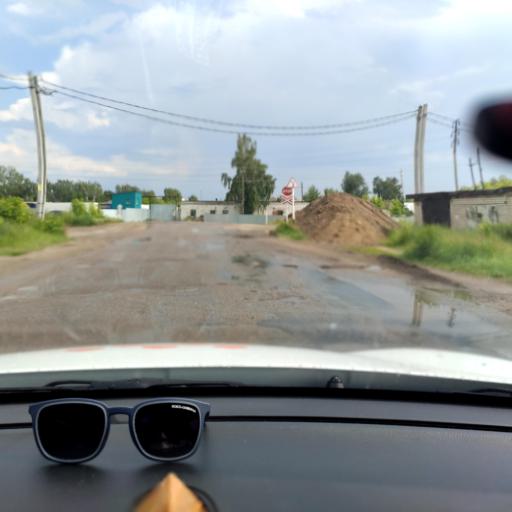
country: RU
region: Tatarstan
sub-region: Zelenodol'skiy Rayon
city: Vasil'yevo
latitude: 55.8357
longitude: 48.6829
